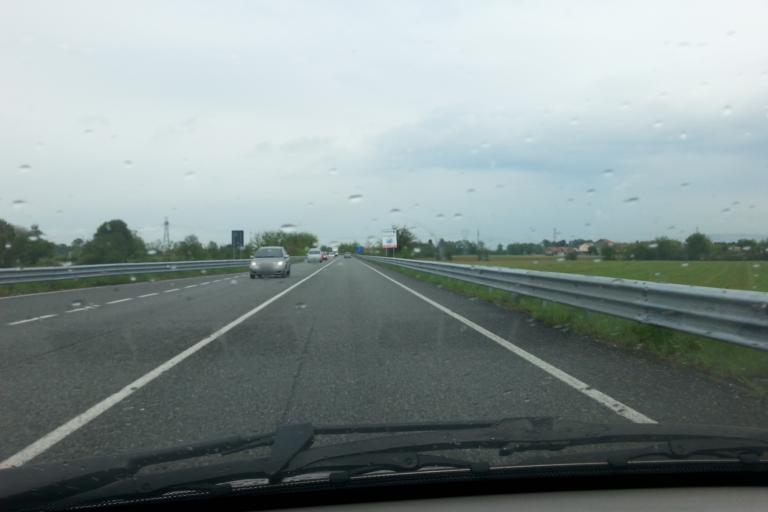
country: IT
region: Piedmont
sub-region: Provincia di Torino
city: Alpignano
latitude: 45.1204
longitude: 7.5252
